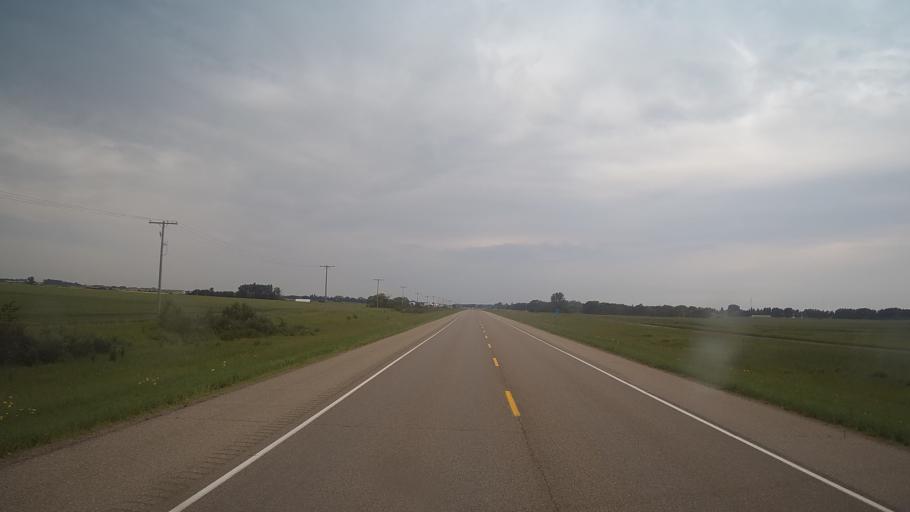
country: CA
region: Saskatchewan
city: Langham
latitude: 52.1289
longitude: -107.2031
